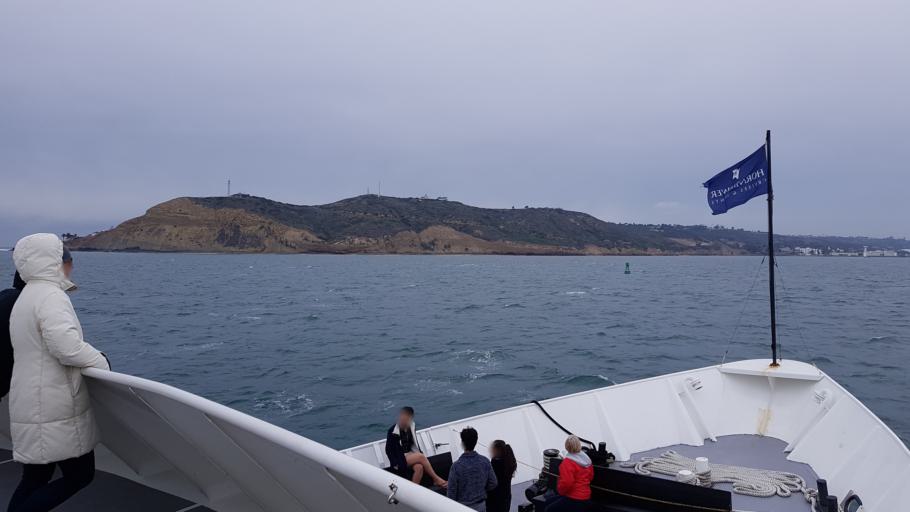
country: US
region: California
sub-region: San Diego County
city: Coronado
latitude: 32.6627
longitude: -117.2272
